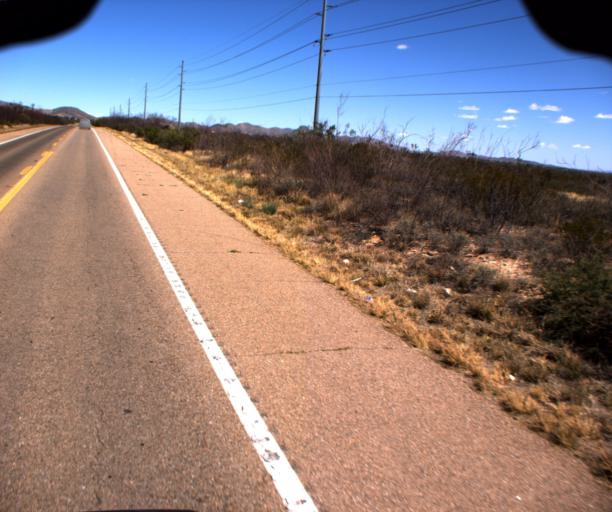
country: US
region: Arizona
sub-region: Cochise County
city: Naco
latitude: 31.3773
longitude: -109.9666
